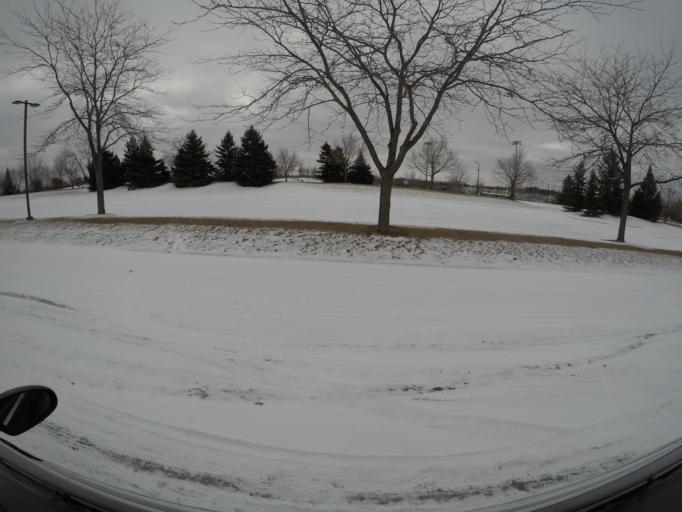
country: US
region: Minnesota
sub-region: Hennepin County
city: Eden Prairie
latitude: 44.8532
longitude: -93.4892
